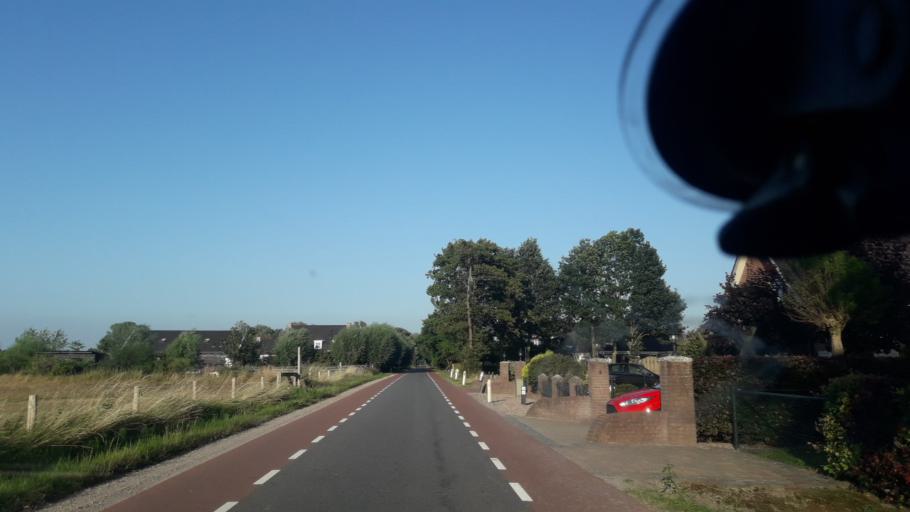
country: NL
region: Utrecht
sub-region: Gemeente Veenendaal
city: Veenendaal
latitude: 52.0139
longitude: 5.5902
